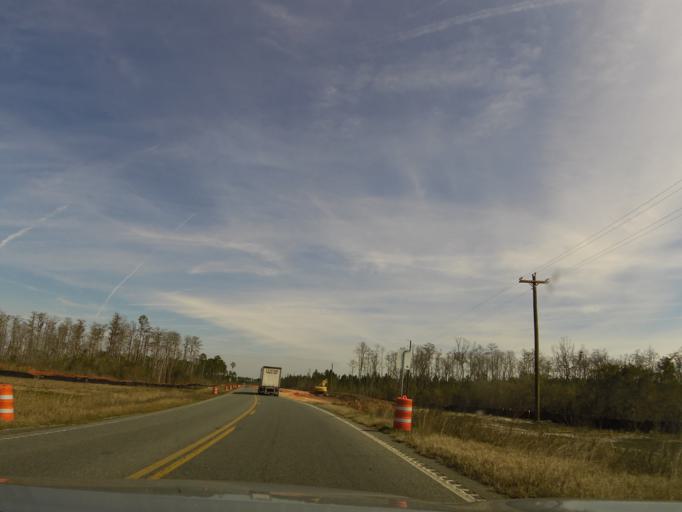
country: US
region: Georgia
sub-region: Ware County
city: Deenwood
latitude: 31.1399
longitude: -82.4807
